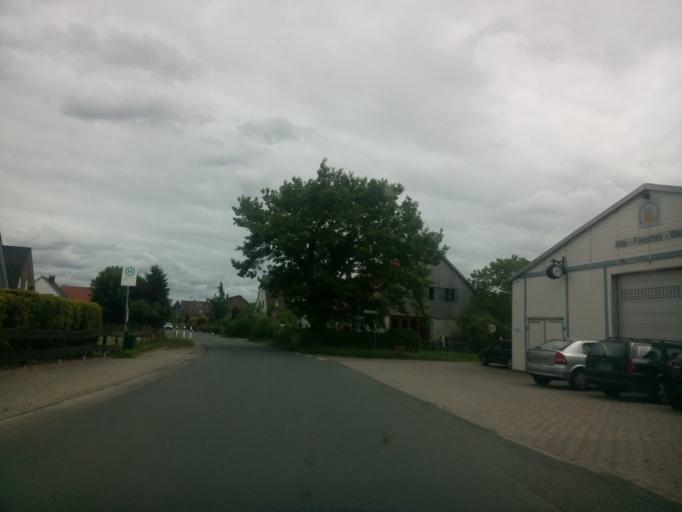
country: DE
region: Lower Saxony
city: Lemwerder
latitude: 53.1755
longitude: 8.5631
